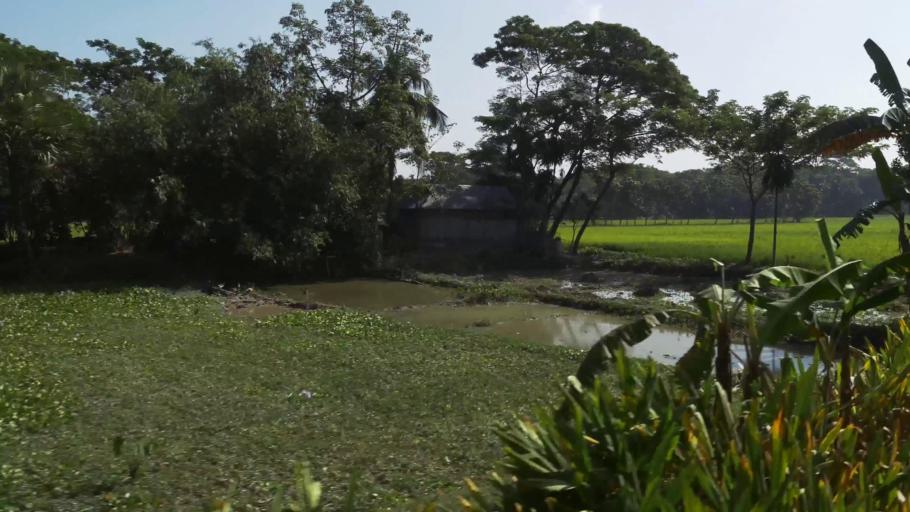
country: BD
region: Dhaka
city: Gafargaon
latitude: 24.5147
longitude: 90.5122
